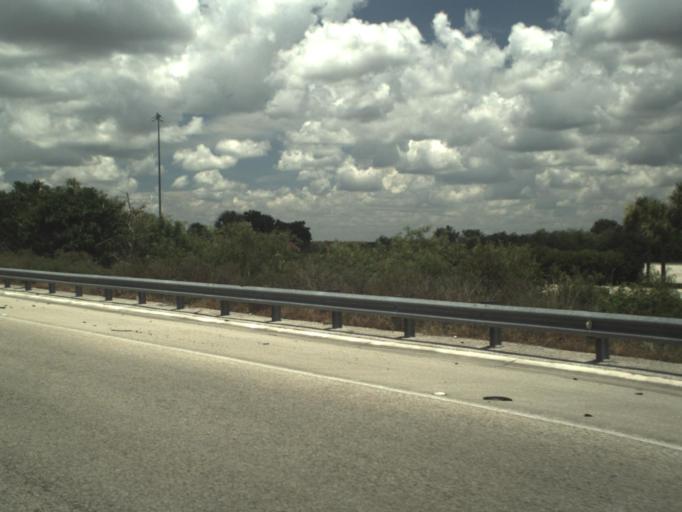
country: US
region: Florida
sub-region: Broward County
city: Weston
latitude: 26.1466
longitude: -80.6293
